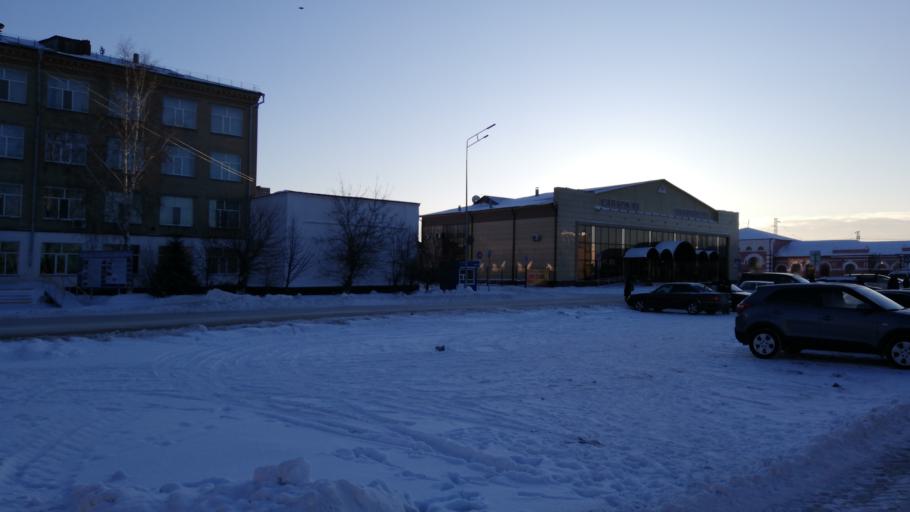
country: KZ
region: Soltustik Qazaqstan
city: Petropavlovsk
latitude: 54.8576
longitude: 69.1712
